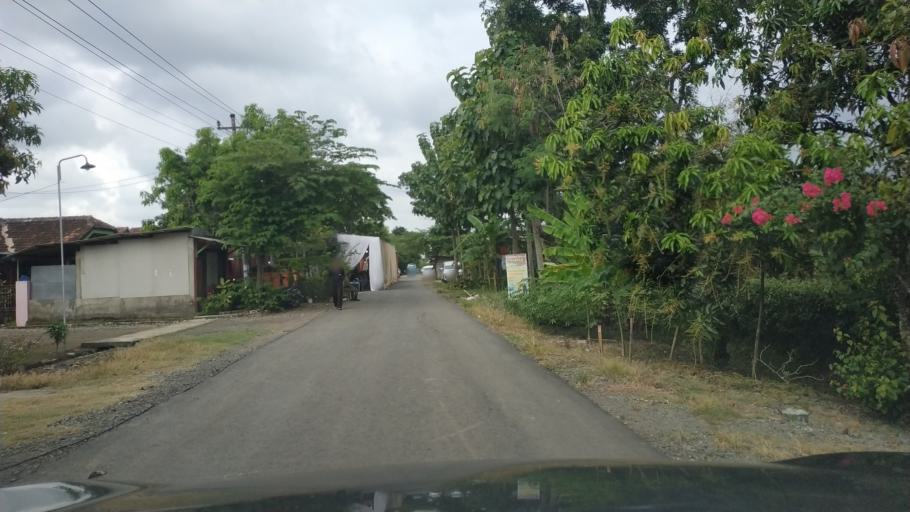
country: ID
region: Central Java
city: Pemalang
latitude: -6.9478
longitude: 109.3438
